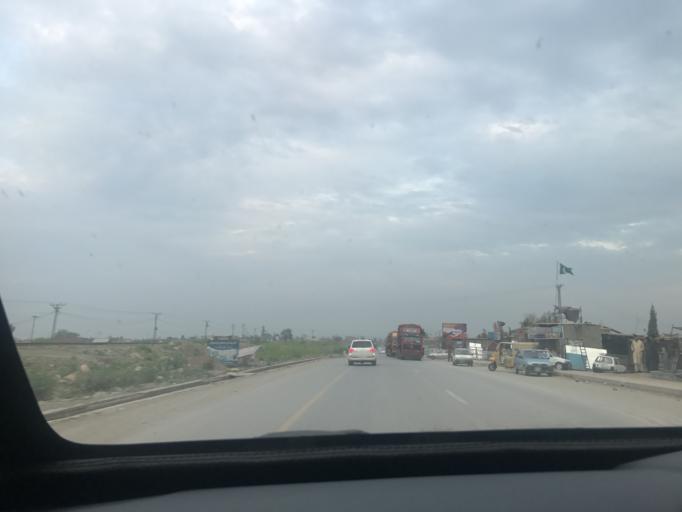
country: PK
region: Khyber Pakhtunkhwa
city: Peshawar
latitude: 33.9995
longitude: 71.3916
